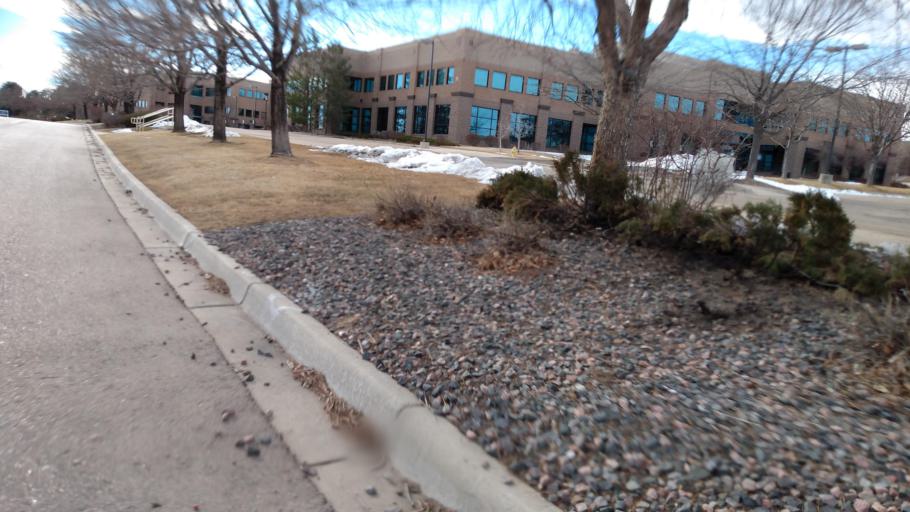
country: US
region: Colorado
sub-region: Boulder County
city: Superior
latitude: 39.9645
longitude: -105.1694
